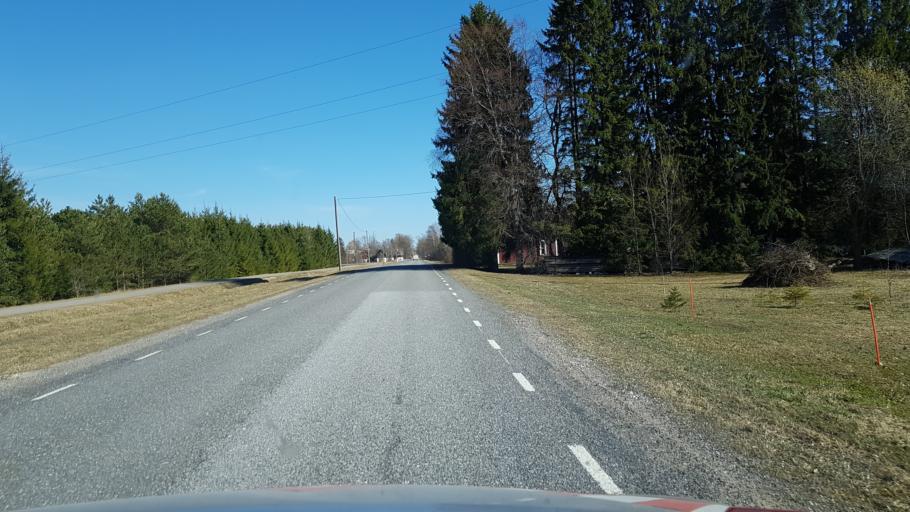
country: EE
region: Laeaene-Virumaa
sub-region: Rakke vald
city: Rakke
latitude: 58.9945
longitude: 26.2198
